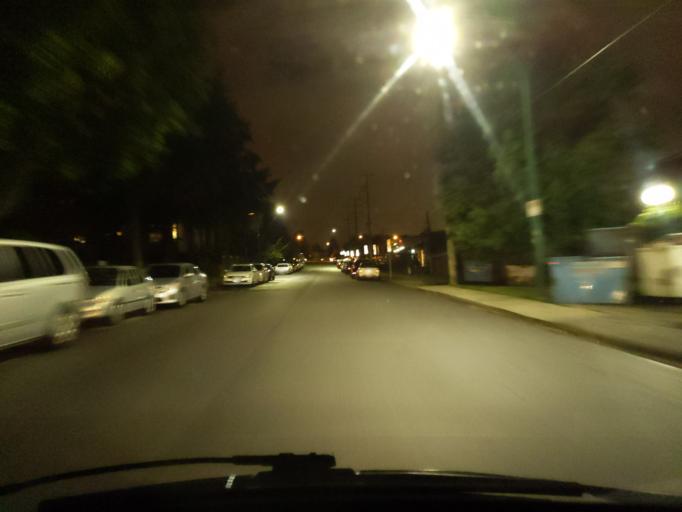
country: CA
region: British Columbia
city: Burnaby
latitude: 49.2543
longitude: -123.0210
